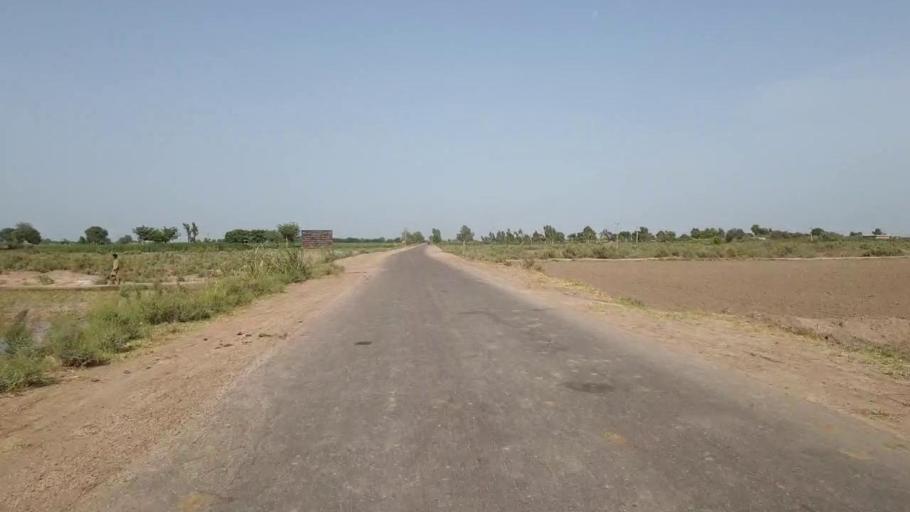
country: PK
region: Sindh
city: Sakrand
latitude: 26.2845
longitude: 68.2459
